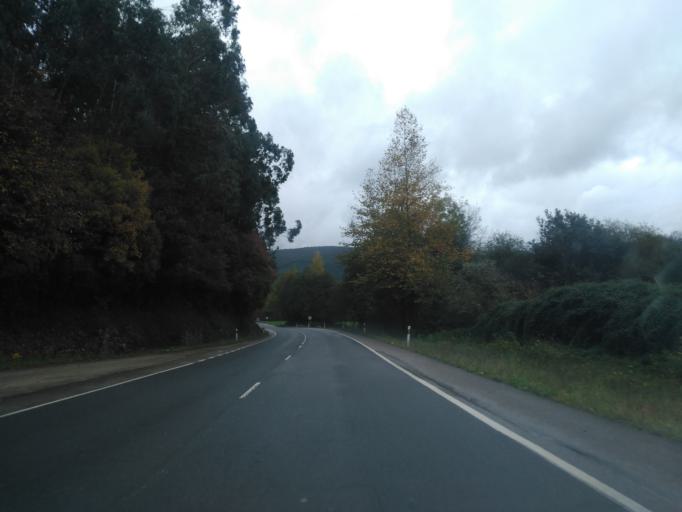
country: ES
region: Cantabria
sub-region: Provincia de Cantabria
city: Puente Viesgo
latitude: 43.3099
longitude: -3.9601
